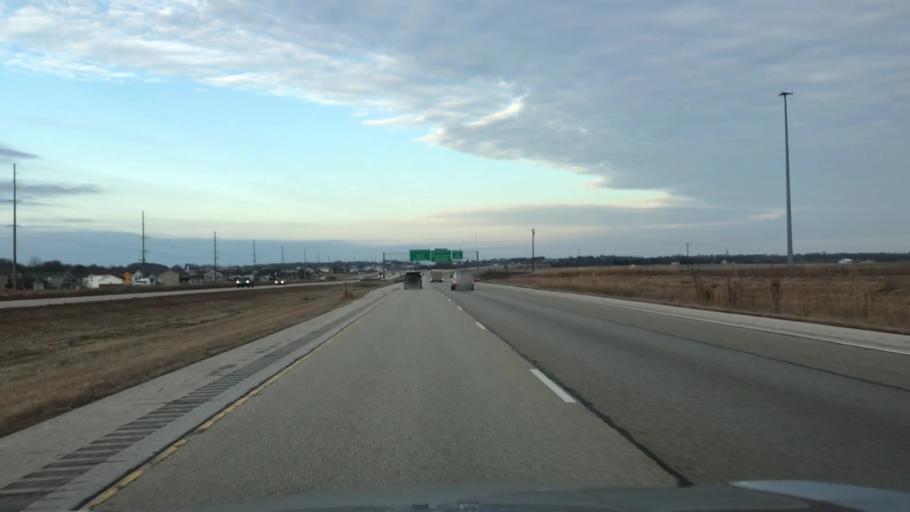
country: US
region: Illinois
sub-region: McLean County
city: Bloomington
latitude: 40.4281
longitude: -89.0362
